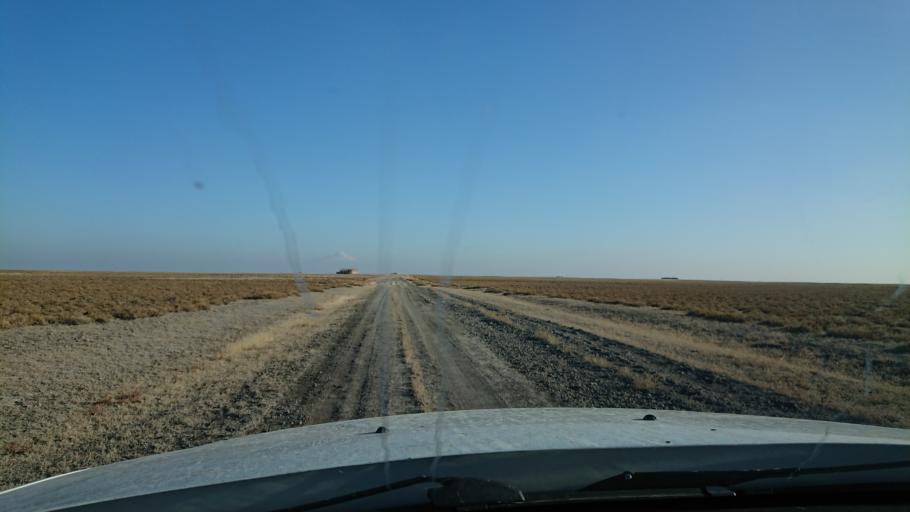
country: TR
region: Aksaray
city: Sultanhani
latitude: 38.3960
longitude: 33.5896
